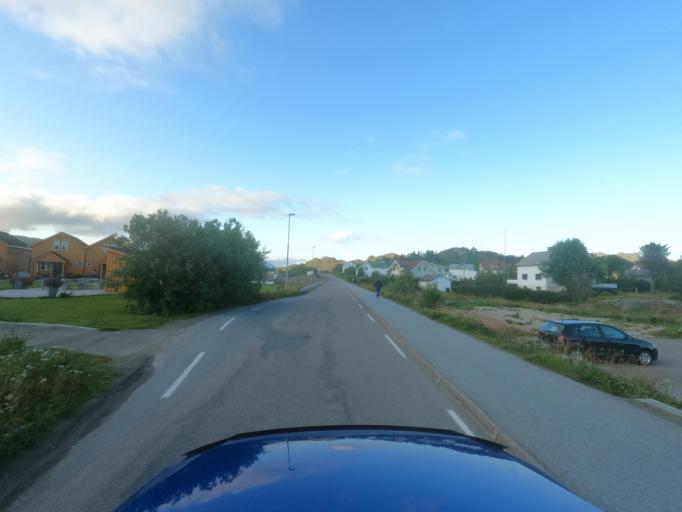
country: NO
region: Nordland
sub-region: Vestvagoy
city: Gravdal
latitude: 68.0760
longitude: 13.5431
